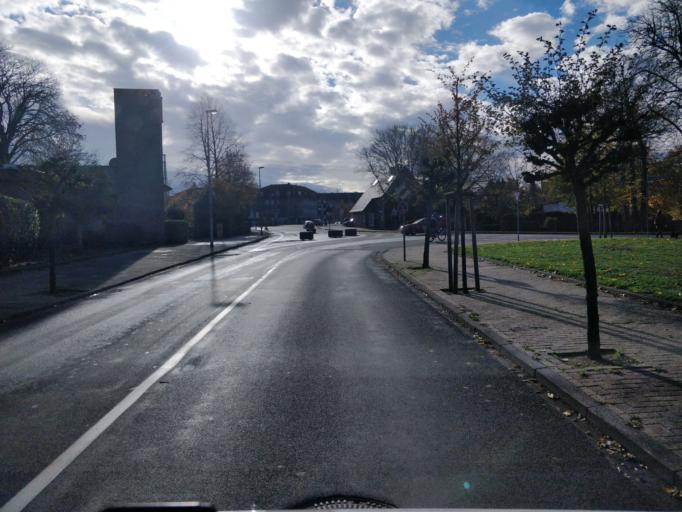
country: DE
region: North Rhine-Westphalia
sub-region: Regierungsbezirk Dusseldorf
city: Emmerich
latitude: 51.8366
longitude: 6.2473
